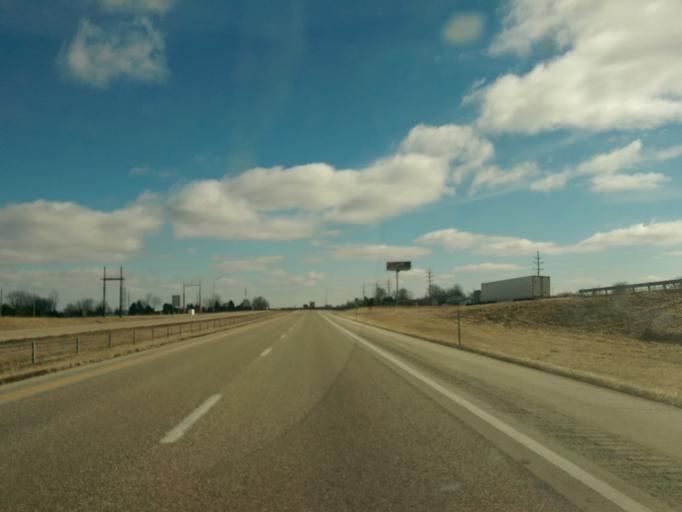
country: US
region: Missouri
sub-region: Montgomery County
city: Montgomery City
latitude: 38.8734
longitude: -91.3728
